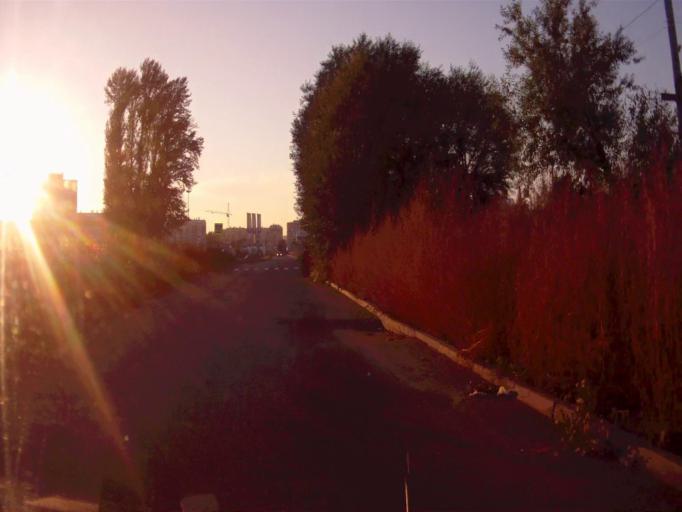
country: RU
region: Chelyabinsk
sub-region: Gorod Chelyabinsk
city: Chelyabinsk
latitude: 55.1753
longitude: 61.3791
